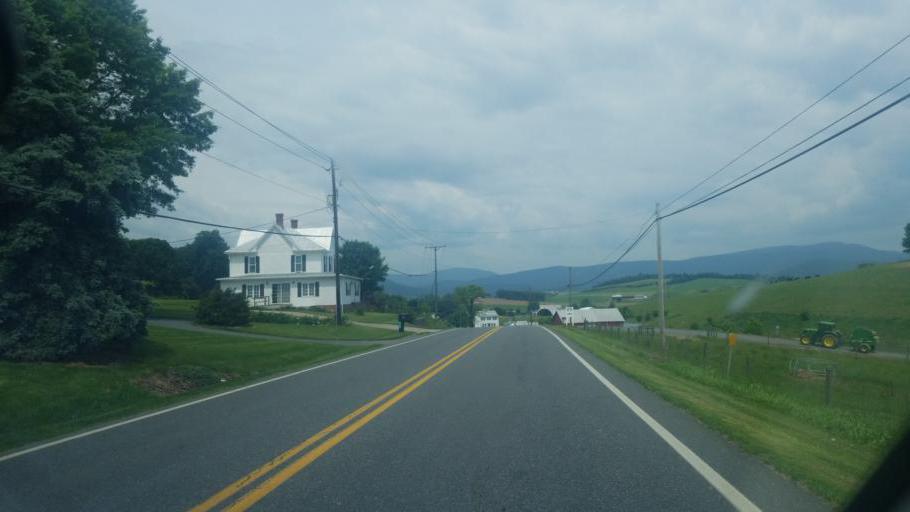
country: US
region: Virginia
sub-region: Rockingham County
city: Dayton
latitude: 38.4628
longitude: -78.9622
